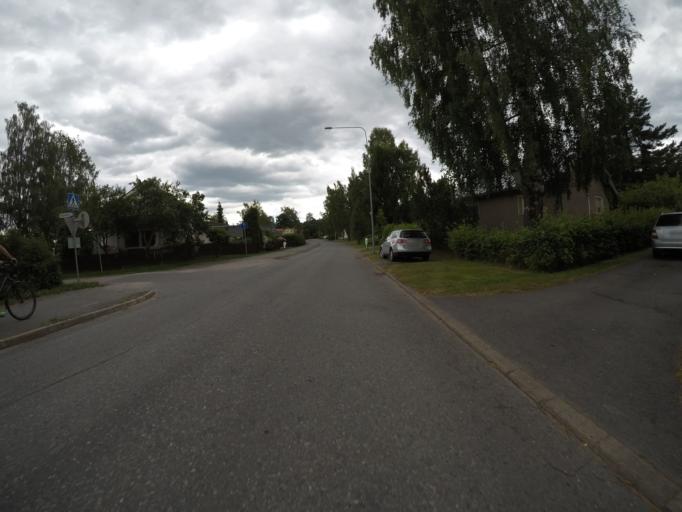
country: FI
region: Haeme
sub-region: Haemeenlinna
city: Haemeenlinna
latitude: 60.9827
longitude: 24.4396
